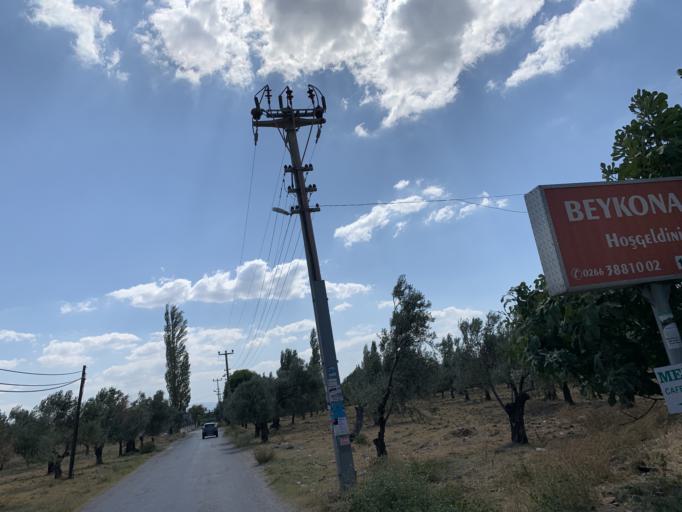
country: TR
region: Balikesir
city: Altinoluk
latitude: 39.5672
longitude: 26.8356
